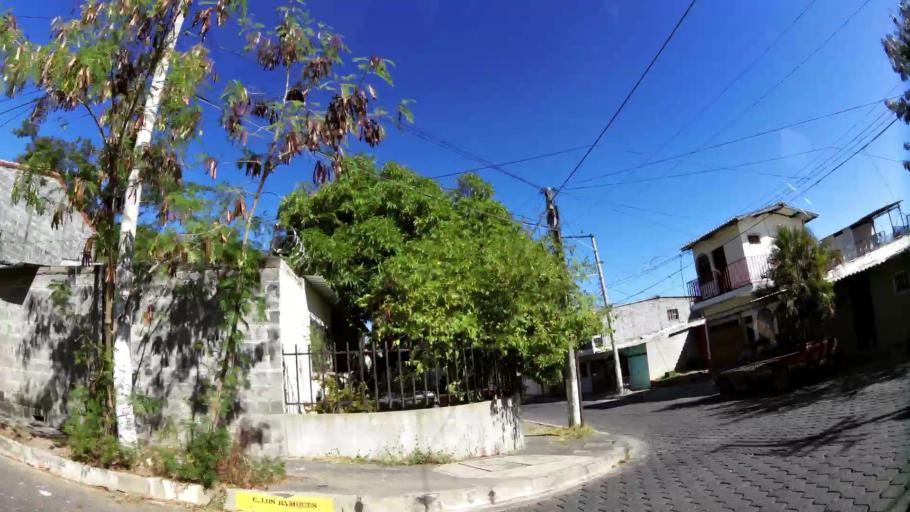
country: SV
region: San Miguel
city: San Miguel
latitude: 13.4624
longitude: -88.1615
